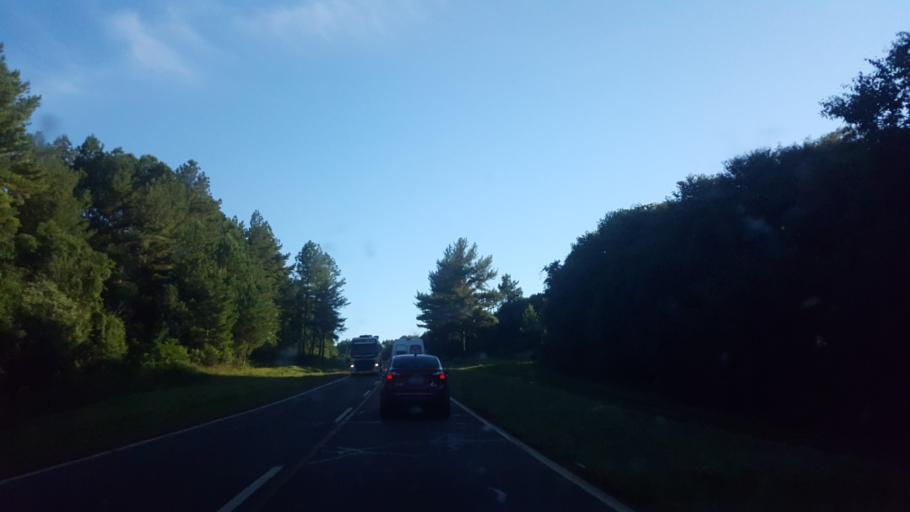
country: AR
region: Misiones
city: El Alcazar
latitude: -26.7627
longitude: -54.8883
